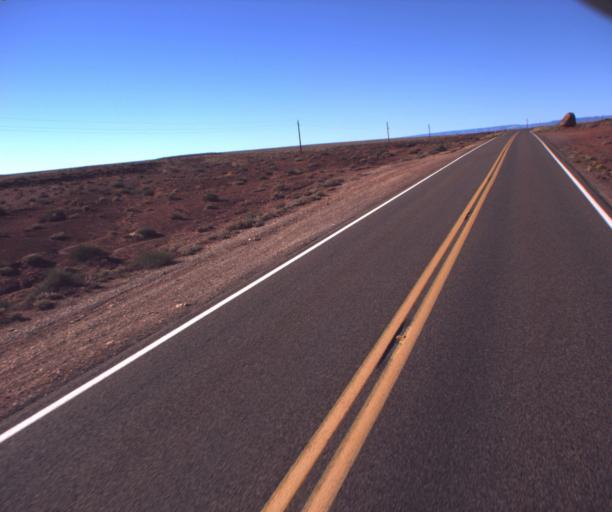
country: US
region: Arizona
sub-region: Coconino County
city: Page
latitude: 36.7560
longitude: -111.7162
